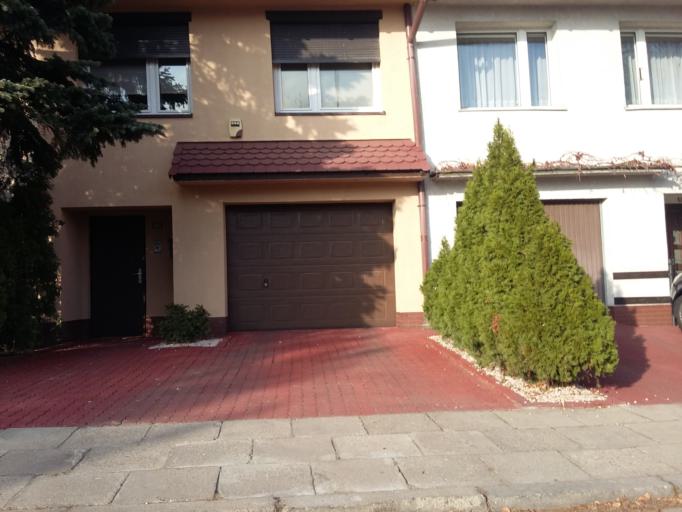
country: PL
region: Lodz Voivodeship
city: Lodz
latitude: 51.7394
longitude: 19.4126
